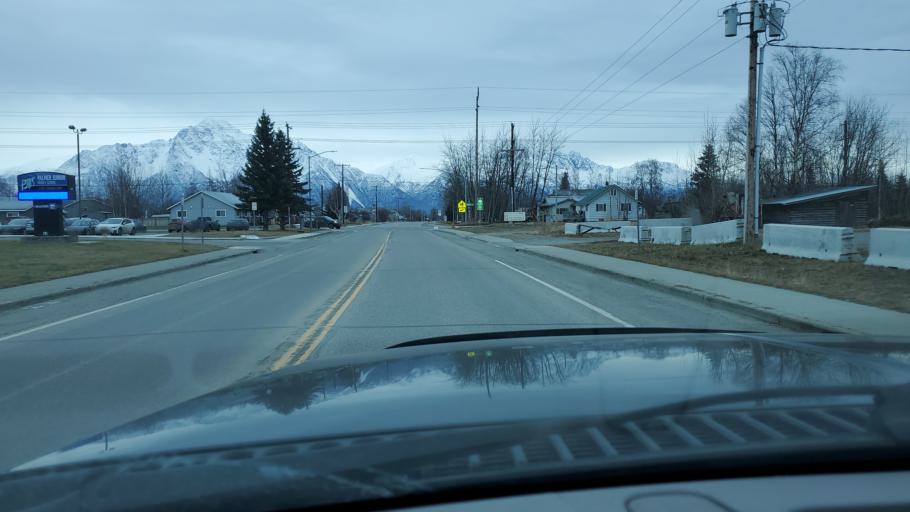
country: US
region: Alaska
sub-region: Matanuska-Susitna Borough
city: Palmer
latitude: 61.5931
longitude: -149.1108
